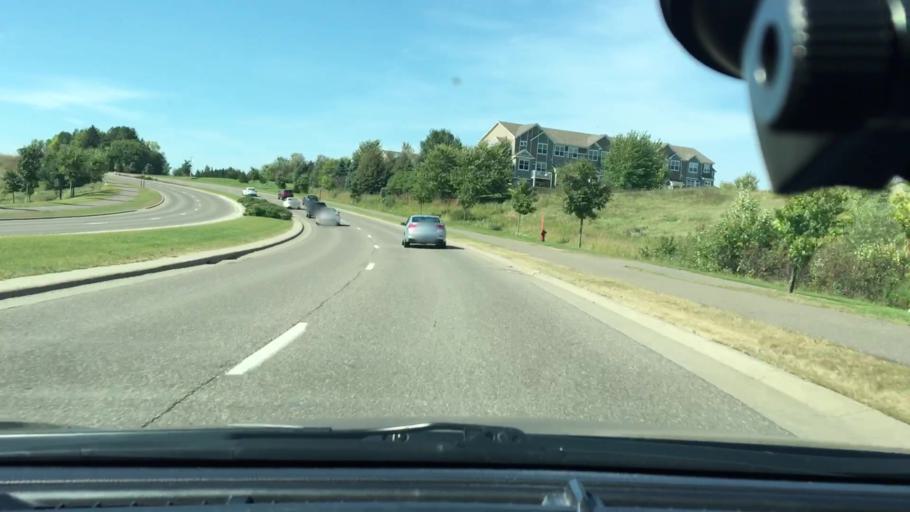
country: US
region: Minnesota
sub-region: Hennepin County
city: Maple Grove
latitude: 45.0846
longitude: -93.4933
